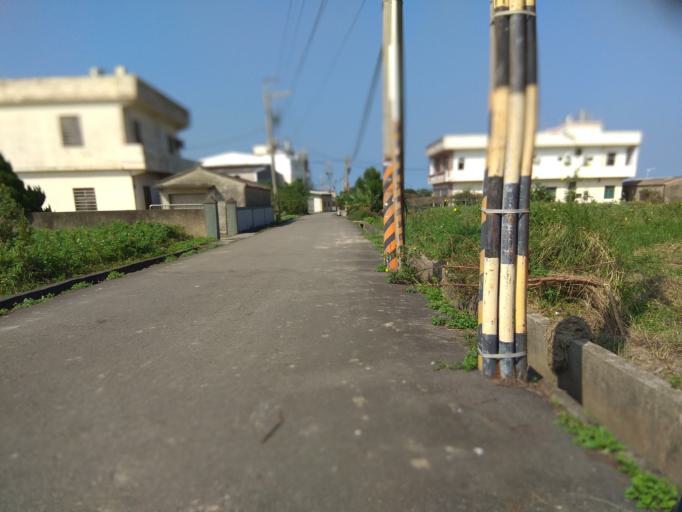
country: TW
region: Taiwan
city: Taoyuan City
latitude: 25.0470
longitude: 121.2165
